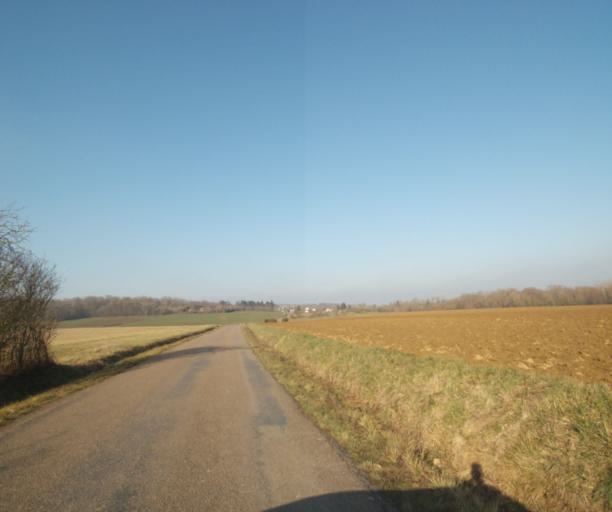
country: FR
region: Champagne-Ardenne
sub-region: Departement de la Haute-Marne
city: Wassy
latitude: 48.5038
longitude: 4.9259
